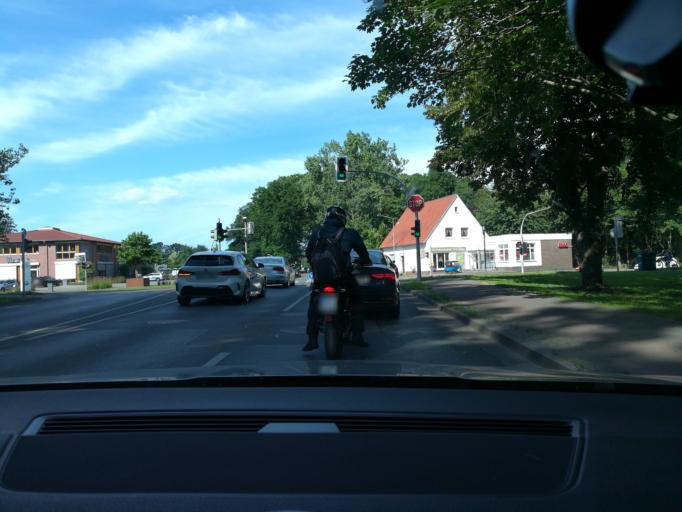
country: DE
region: North Rhine-Westphalia
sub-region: Regierungsbezirk Detmold
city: Minden
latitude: 52.3131
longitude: 8.8810
